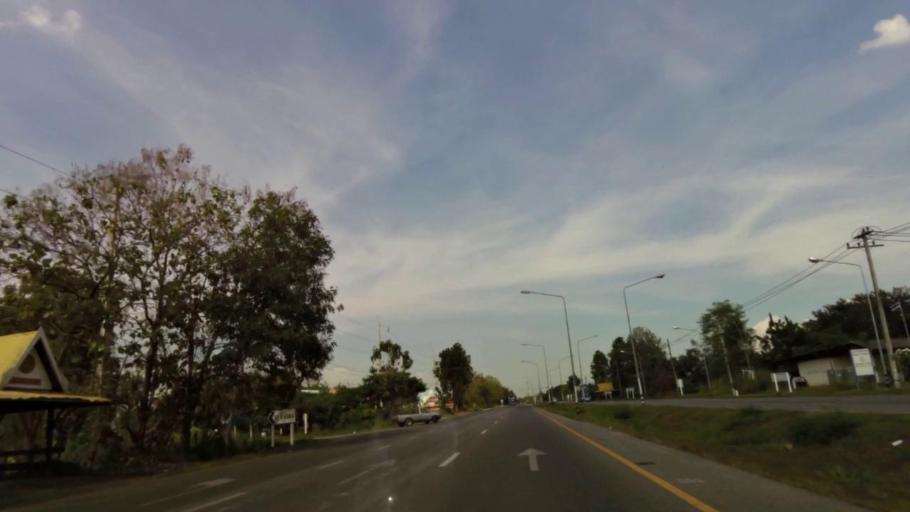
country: TH
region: Uttaradit
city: Tron
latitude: 17.5221
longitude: 100.2170
